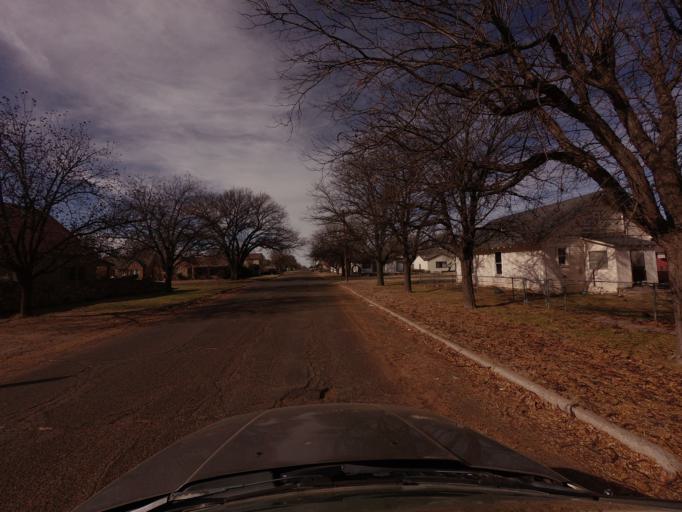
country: US
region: New Mexico
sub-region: Curry County
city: Clovis
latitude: 34.4068
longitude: -103.1973
